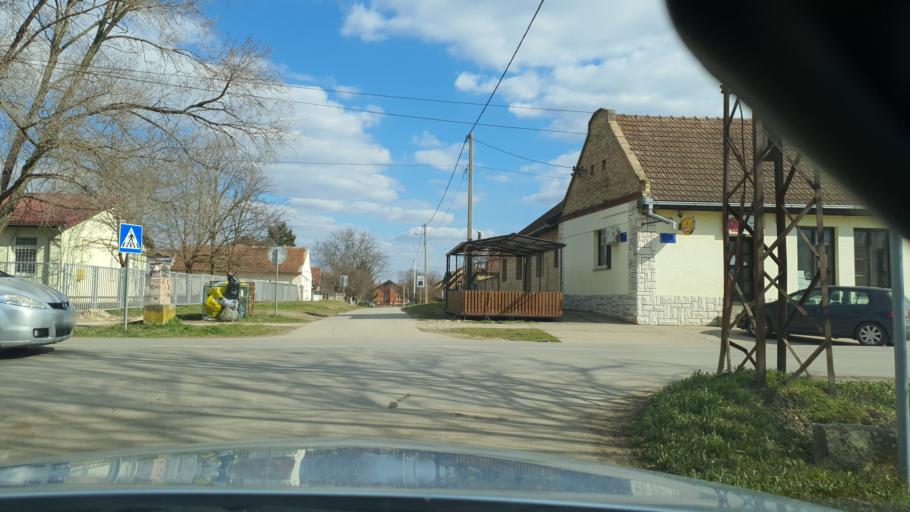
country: RS
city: Kulpin
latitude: 45.4033
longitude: 19.5892
